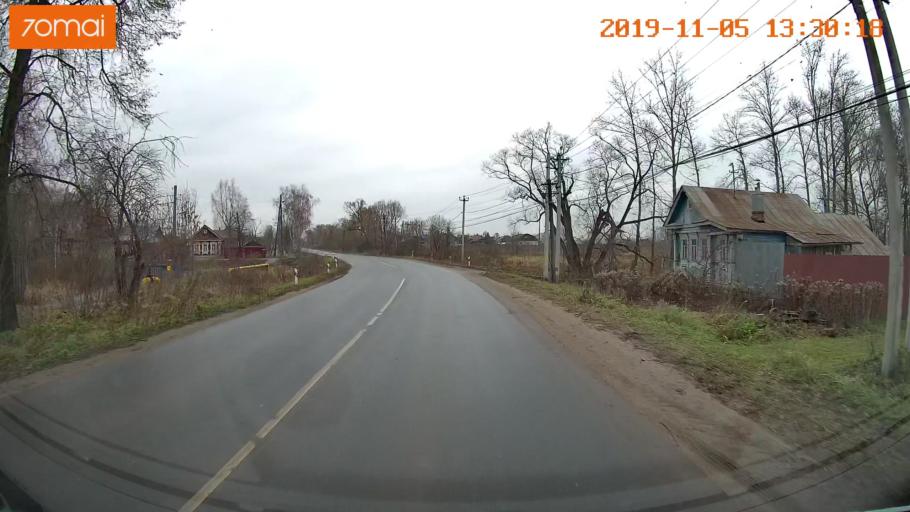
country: RU
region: Ivanovo
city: Shuya
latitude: 56.8661
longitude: 41.3968
